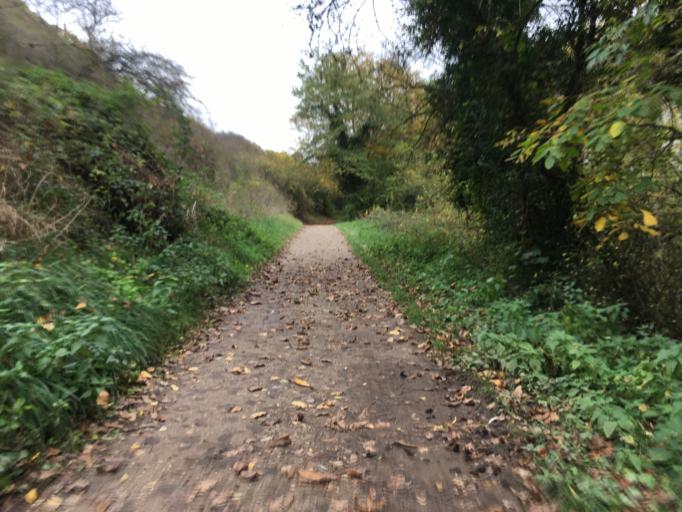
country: DE
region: Baden-Wuerttemberg
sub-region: Freiburg Region
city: Sasbach
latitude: 48.1008
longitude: 7.5930
